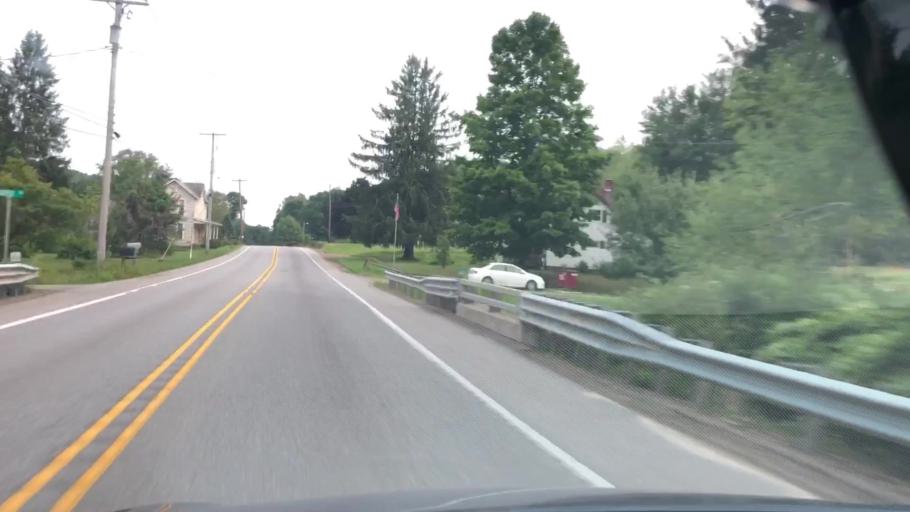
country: US
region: Pennsylvania
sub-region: Venango County
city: Hasson Heights
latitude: 41.5049
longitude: -79.7027
